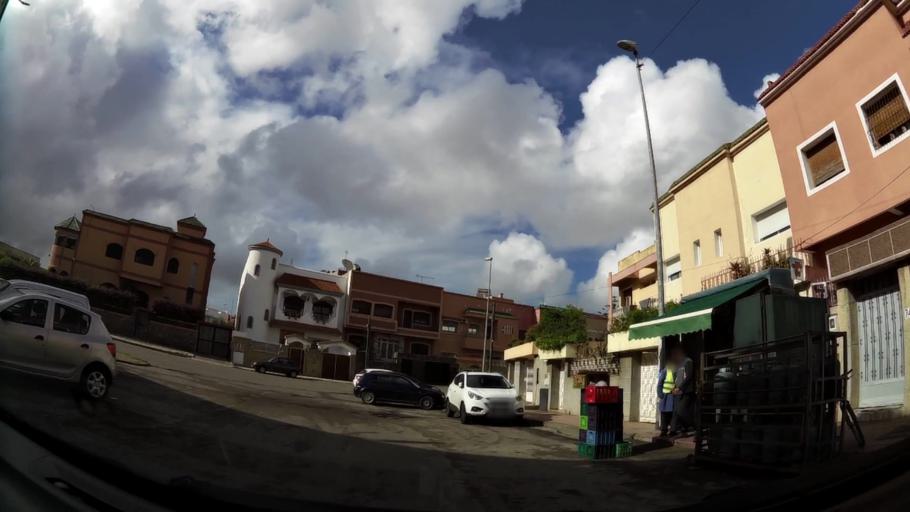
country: MA
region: Grand Casablanca
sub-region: Casablanca
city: Casablanca
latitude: 33.5488
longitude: -7.6030
